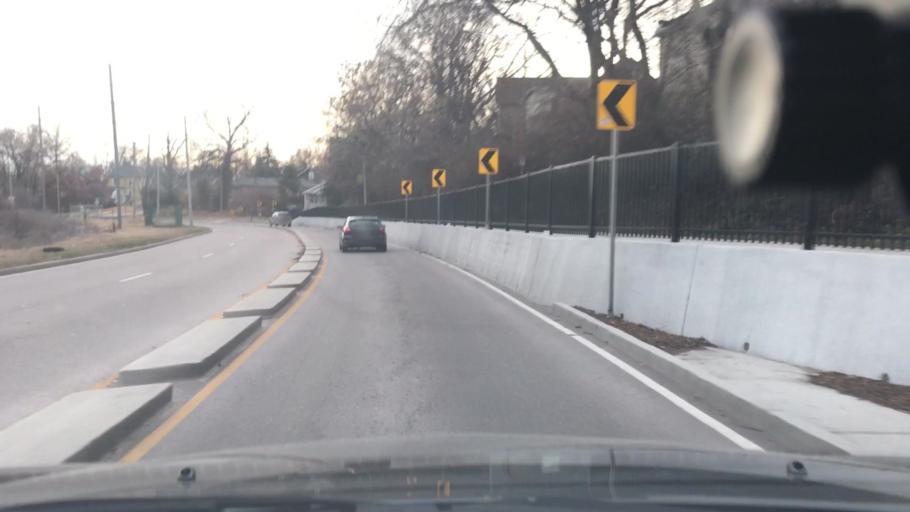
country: US
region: Missouri
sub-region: Saint Louis County
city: Maplewood
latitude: 38.6064
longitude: -90.3137
